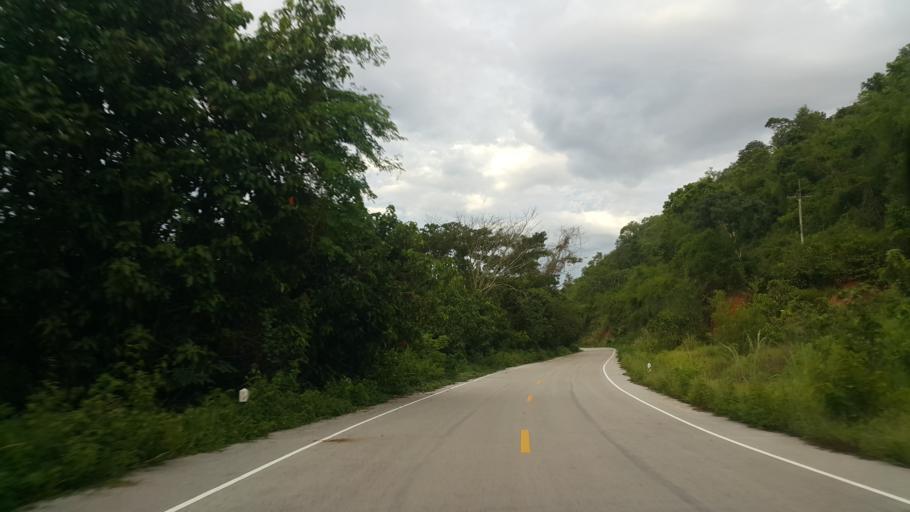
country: TH
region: Loei
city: Na Haeo
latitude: 17.4930
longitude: 101.1000
